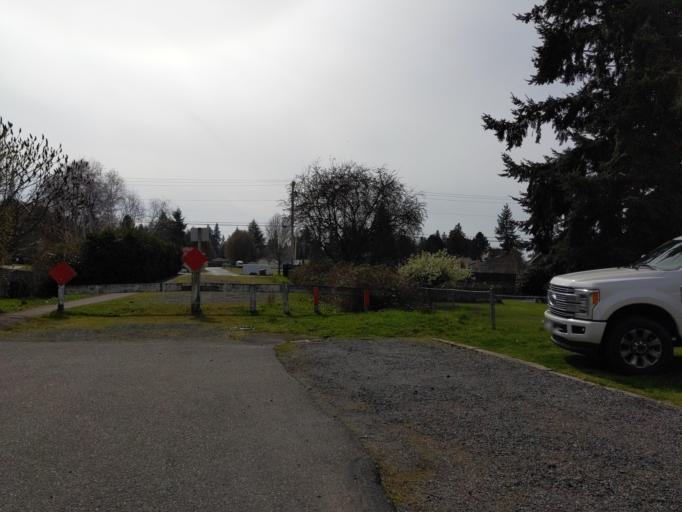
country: US
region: Washington
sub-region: Snohomish County
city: Edmonds
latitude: 47.8185
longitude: -122.3700
